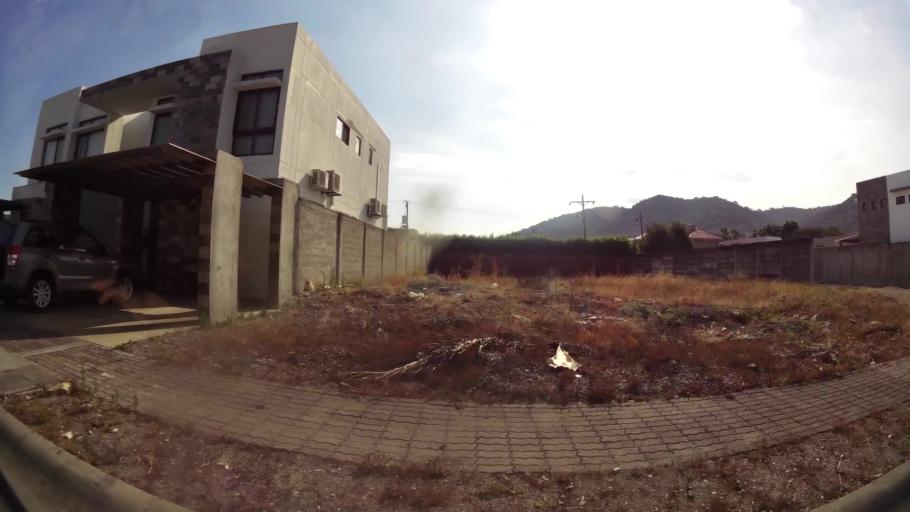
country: EC
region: Guayas
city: Santa Lucia
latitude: -2.1850
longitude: -79.9872
